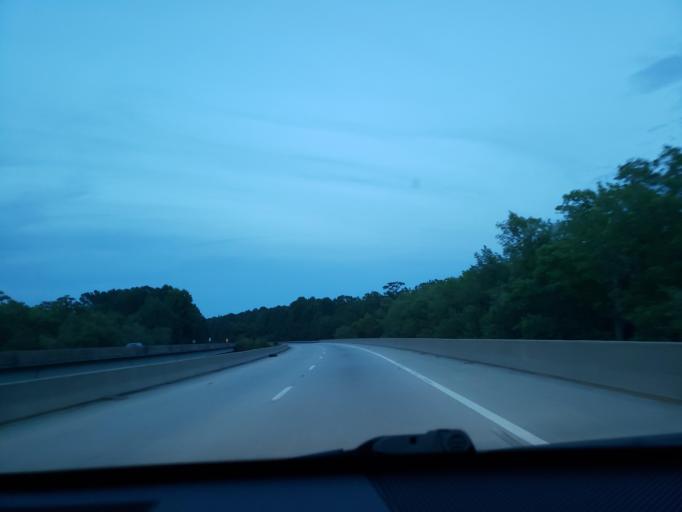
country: US
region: Virginia
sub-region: City of Franklin
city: Franklin
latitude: 36.6396
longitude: -76.8947
